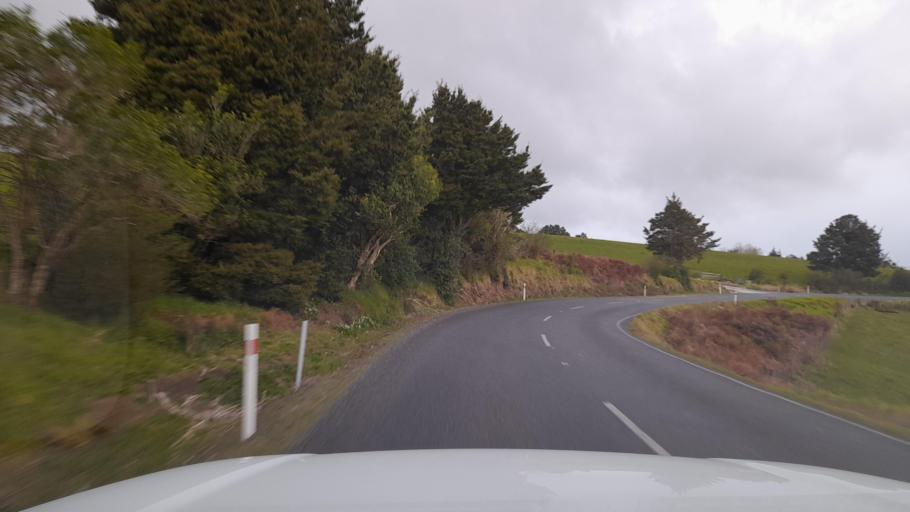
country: NZ
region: Northland
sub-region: Whangarei
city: Maungatapere
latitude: -35.6414
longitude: 174.2186
